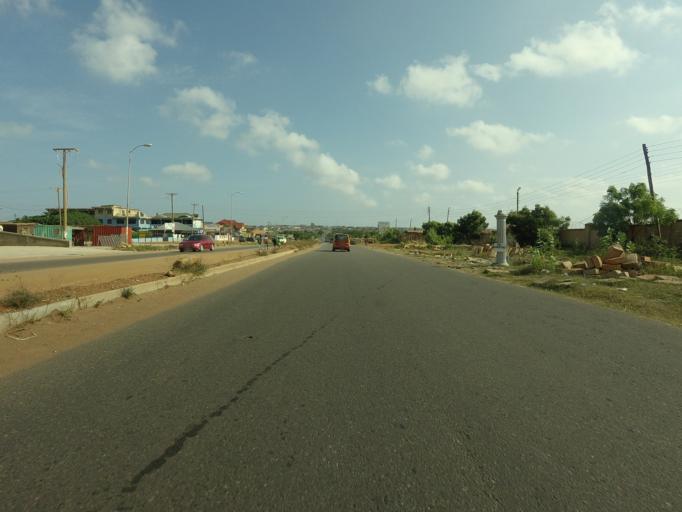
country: GH
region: Greater Accra
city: Tema
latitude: 5.6581
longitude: -0.0528
